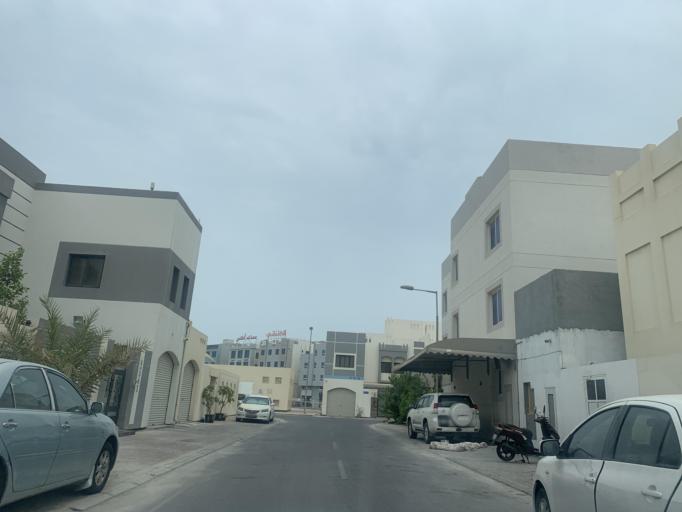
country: BH
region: Muharraq
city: Al Hadd
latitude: 26.2831
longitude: 50.6436
